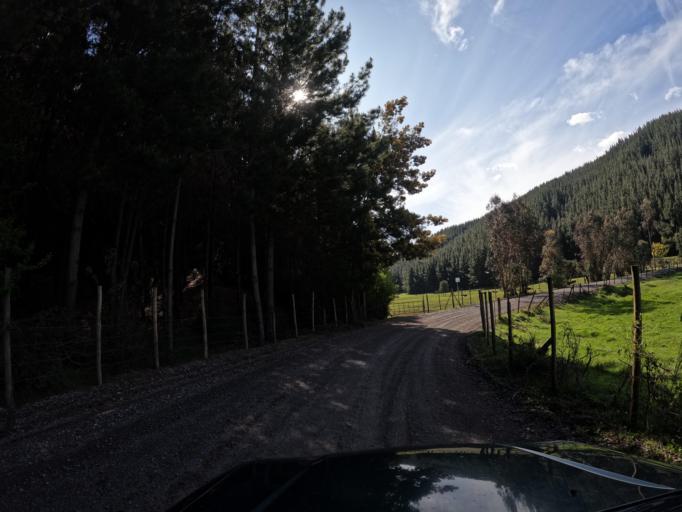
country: CL
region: Biobio
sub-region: Provincia de Concepcion
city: Chiguayante
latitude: -37.0631
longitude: -72.8989
